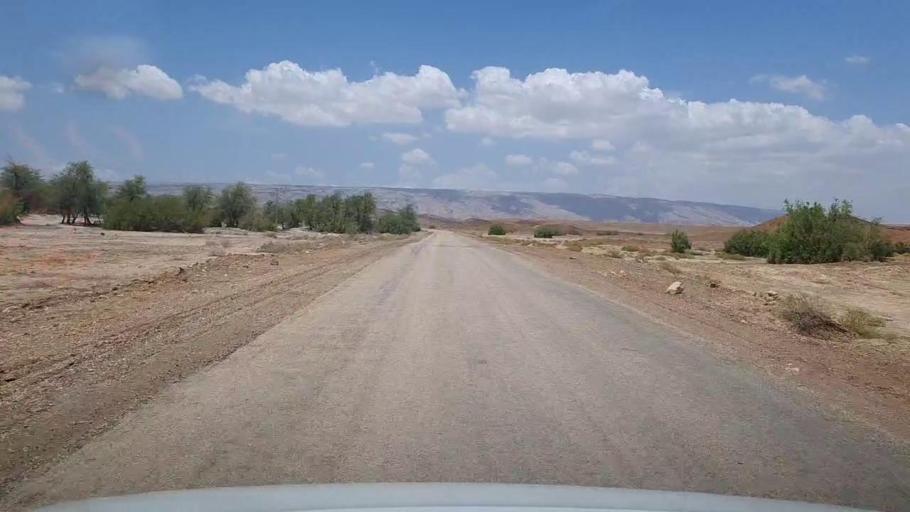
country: PK
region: Sindh
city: Bhan
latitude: 26.3172
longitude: 67.5745
